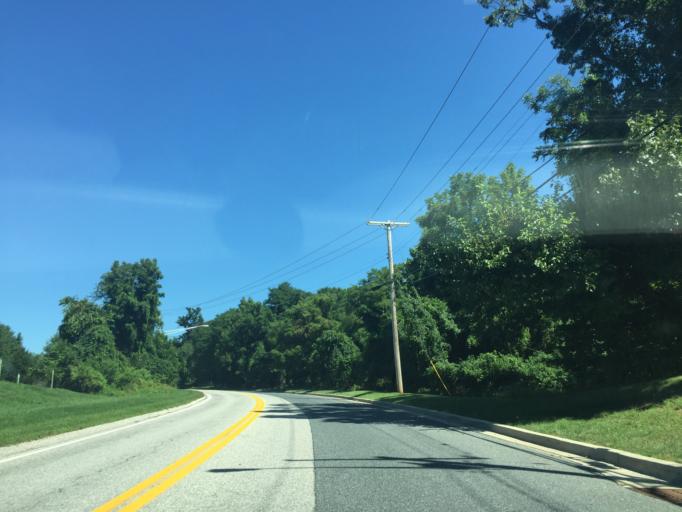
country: US
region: Maryland
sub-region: Baltimore County
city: Timonium
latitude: 39.4599
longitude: -76.6013
